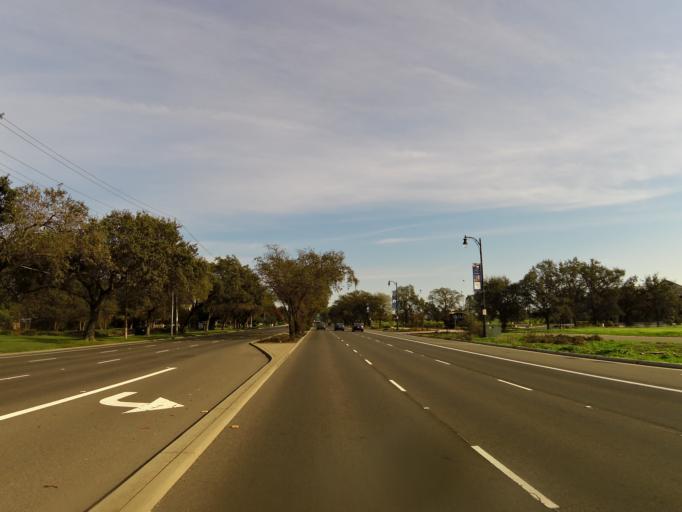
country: US
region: California
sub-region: Sacramento County
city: Laguna
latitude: 38.4090
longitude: -121.4010
